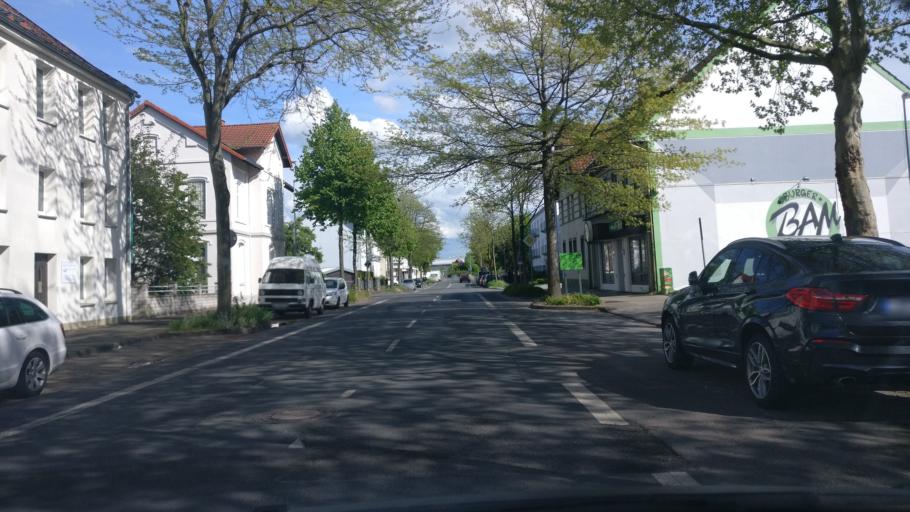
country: DE
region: North Rhine-Westphalia
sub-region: Regierungsbezirk Detmold
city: Lage
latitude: 51.9876
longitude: 8.7994
